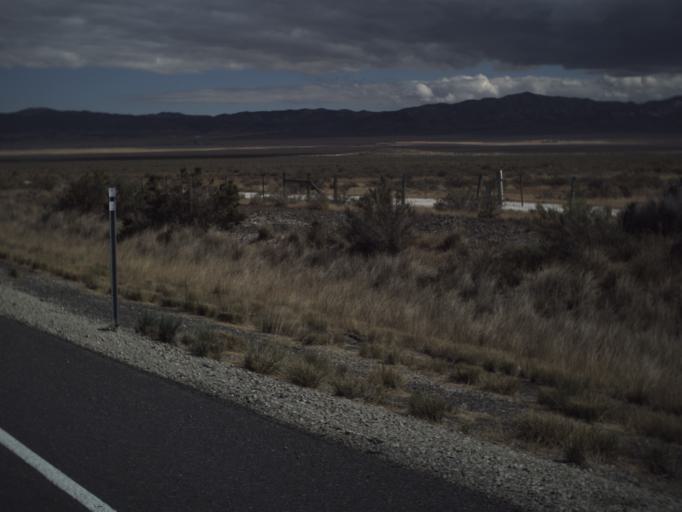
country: US
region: Utah
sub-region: Tooele County
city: Grantsville
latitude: 40.7327
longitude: -113.1091
